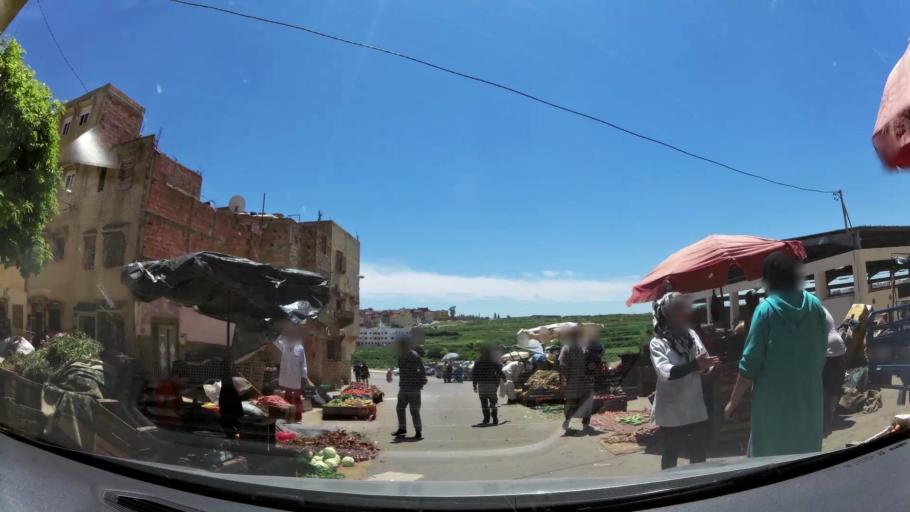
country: MA
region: Meknes-Tafilalet
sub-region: Meknes
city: Meknes
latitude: 33.9079
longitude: -5.5799
